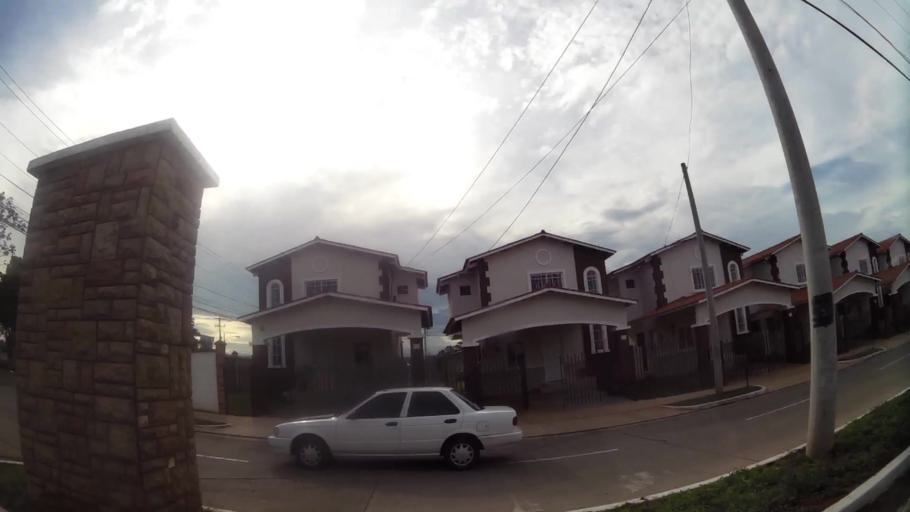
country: PA
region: Panama
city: La Chorrera
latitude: 8.8780
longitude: -79.7660
